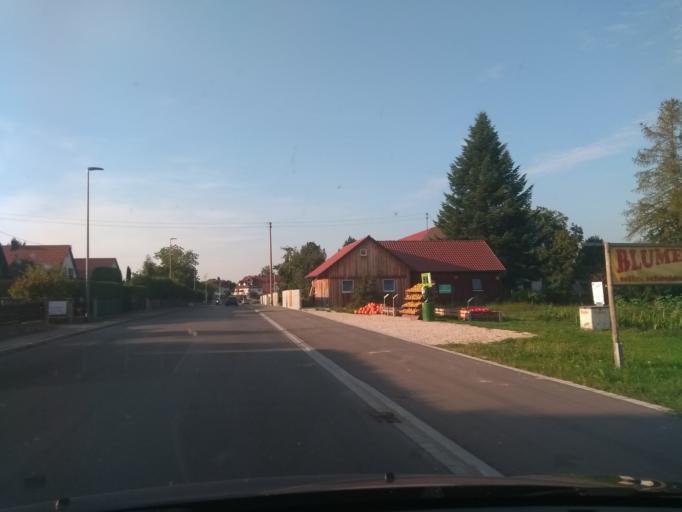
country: DE
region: Bavaria
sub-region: Upper Bavaria
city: Markt Indersdorf
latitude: 48.3503
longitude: 11.3832
